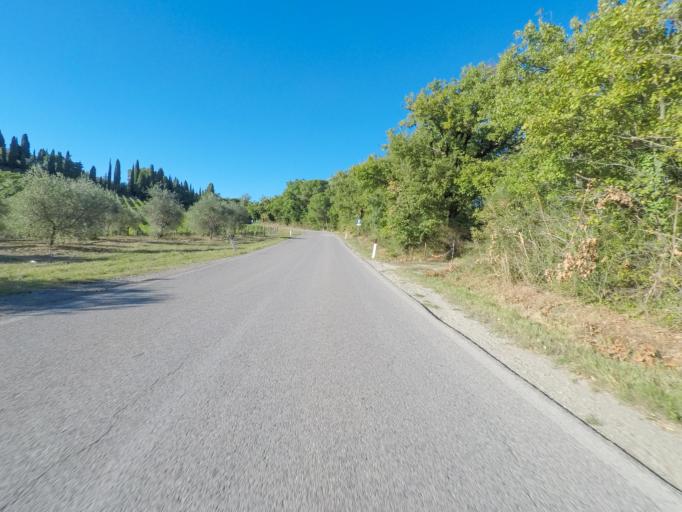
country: IT
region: Tuscany
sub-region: Provincia di Siena
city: Radda in Chianti
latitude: 43.4120
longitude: 11.3519
